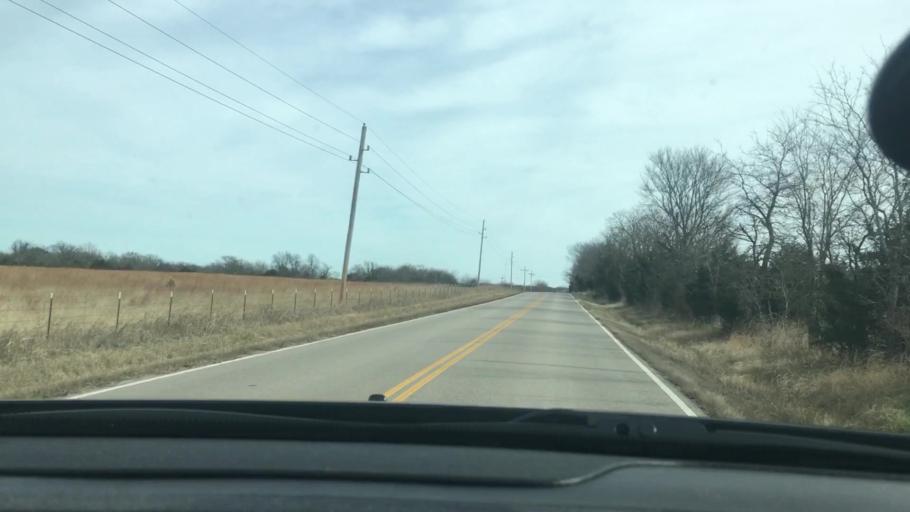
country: US
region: Oklahoma
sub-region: Murray County
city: Sulphur
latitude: 34.4048
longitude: -96.8508
